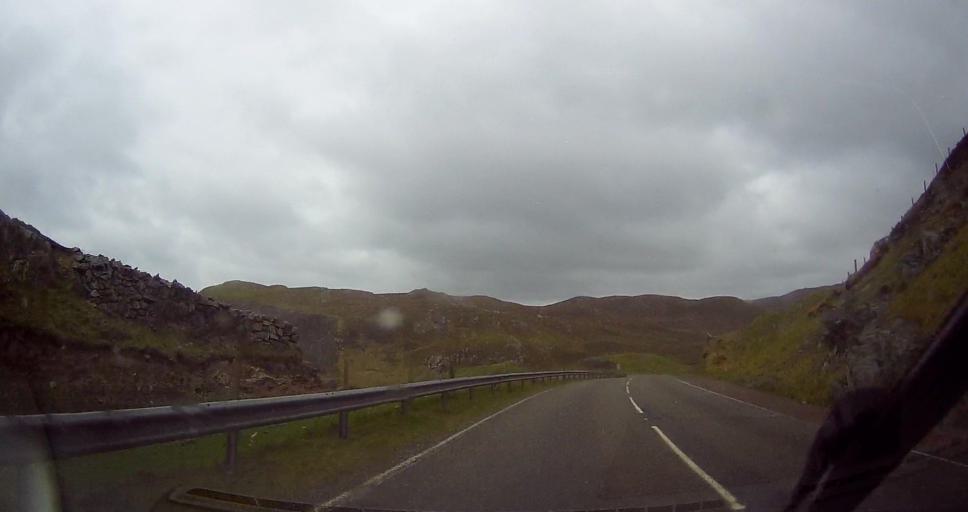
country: GB
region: Scotland
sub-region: Shetland Islands
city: Lerwick
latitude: 60.4007
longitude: -1.3834
